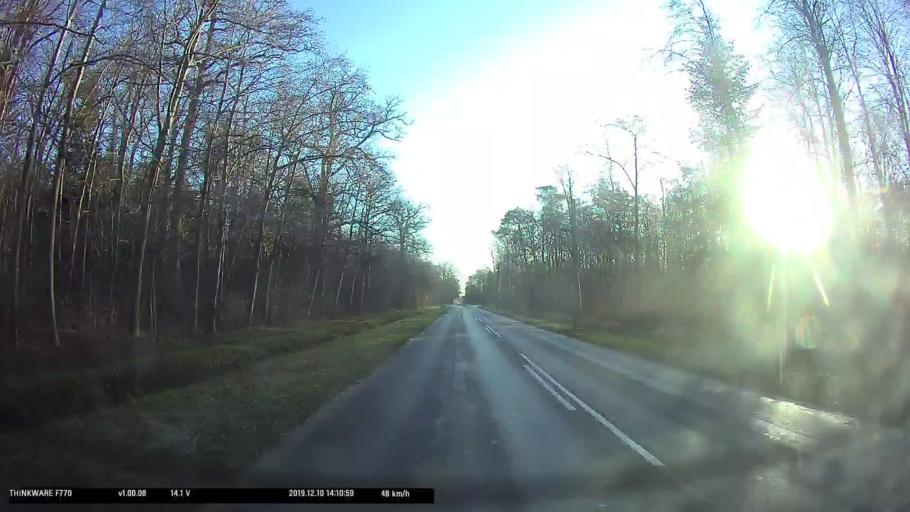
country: DK
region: Capital Region
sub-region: Tarnby Kommune
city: Tarnby
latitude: 55.5765
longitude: 12.5784
